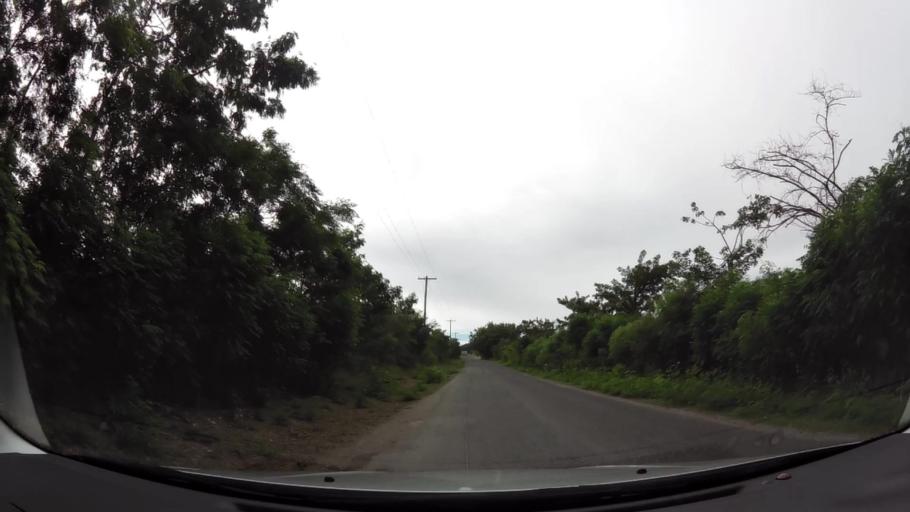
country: AG
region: Saint Peter
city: Parham
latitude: 17.0673
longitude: -61.7341
